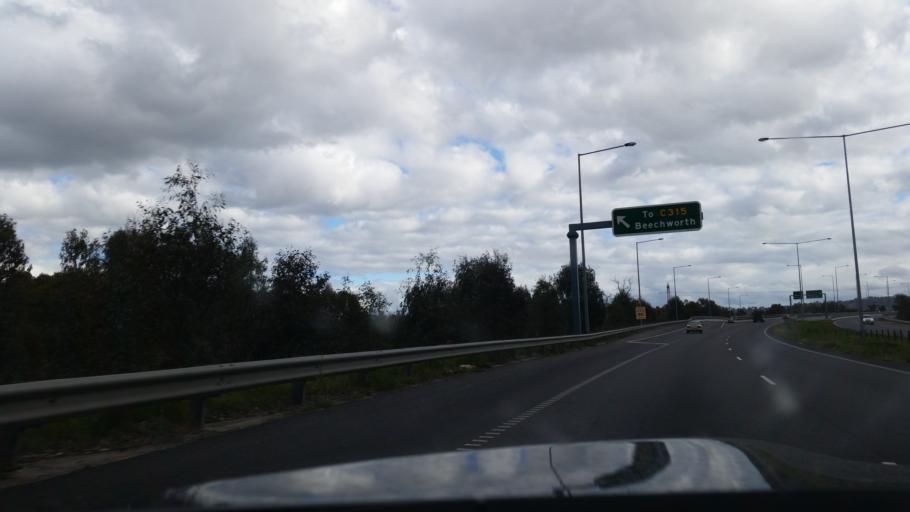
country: AU
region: Victoria
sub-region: Wodonga
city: Wodonga
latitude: -36.1072
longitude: 146.9036
